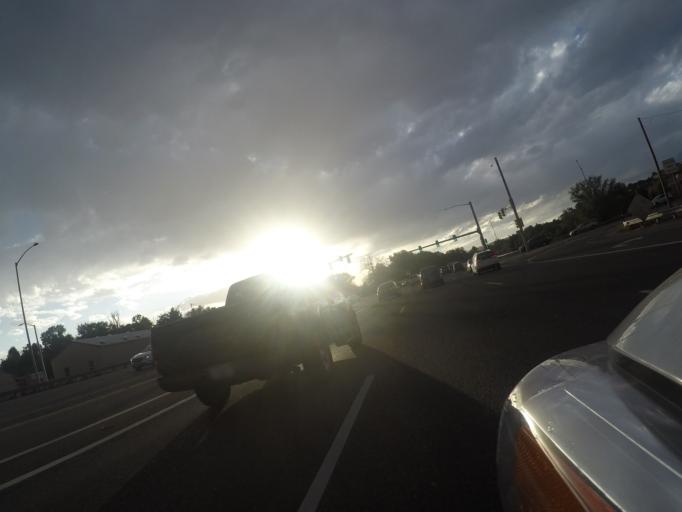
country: US
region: Colorado
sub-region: Arapahoe County
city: Sheridan
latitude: 39.6528
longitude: -105.0317
